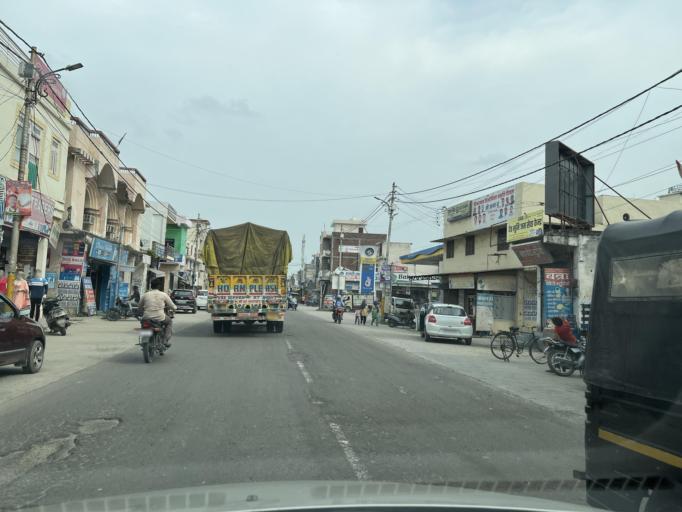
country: IN
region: Uttar Pradesh
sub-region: Rampur
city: Bilaspur
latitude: 29.0427
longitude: 79.2476
